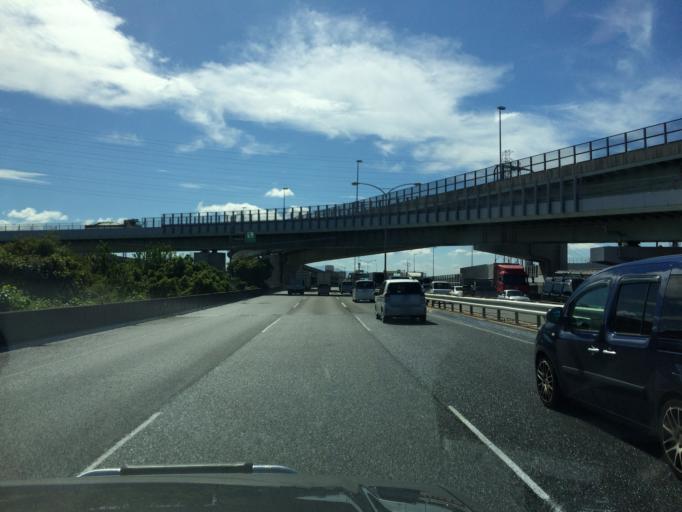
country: JP
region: Osaka
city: Daitocho
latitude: 34.6780
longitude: 135.5972
